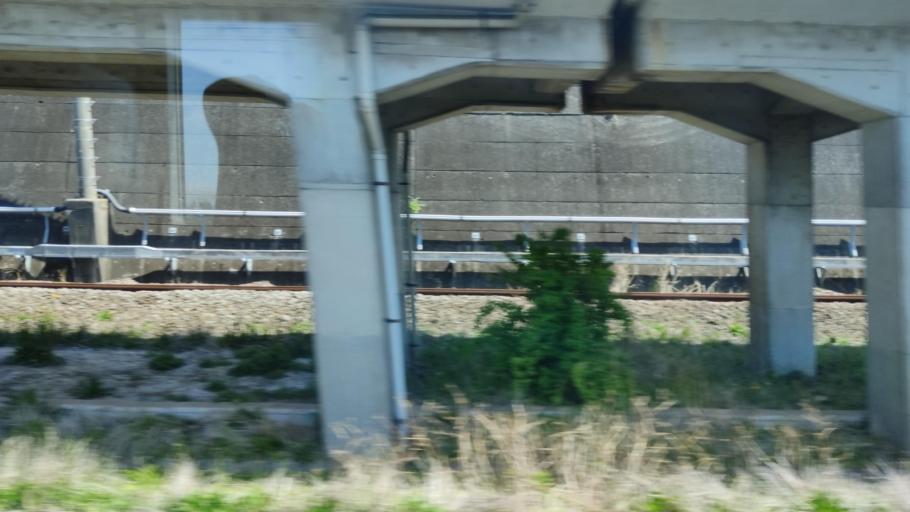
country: JP
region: Kanagawa
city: Kamakura
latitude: 35.3700
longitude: 139.5295
